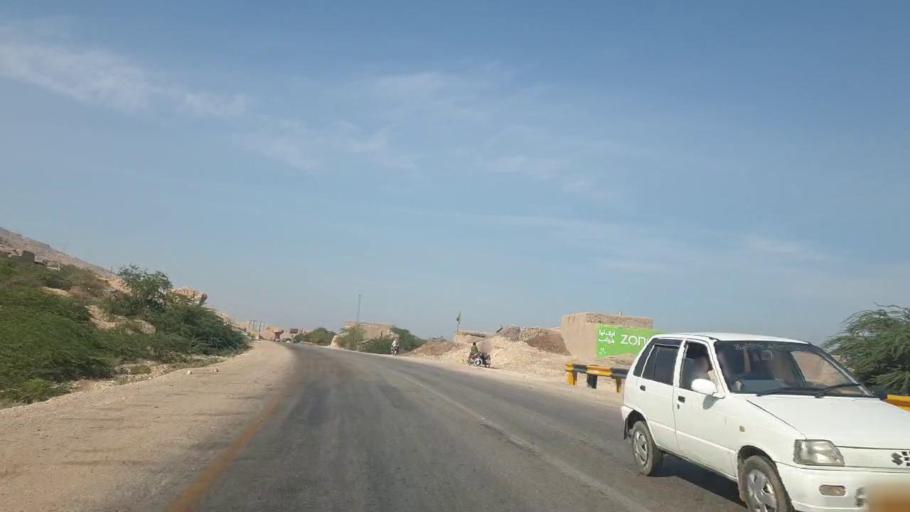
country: PK
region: Sindh
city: Sehwan
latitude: 26.3004
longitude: 67.8949
